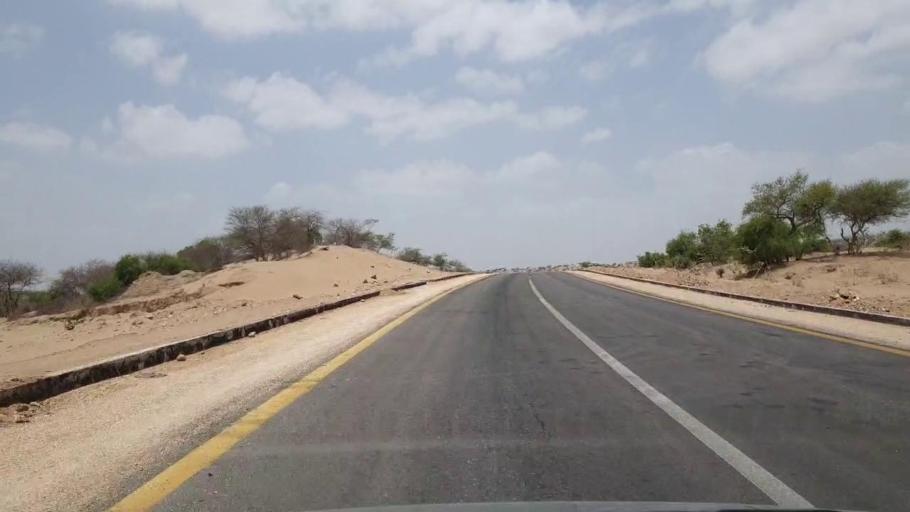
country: PK
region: Sindh
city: Mithi
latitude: 24.8359
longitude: 69.6355
